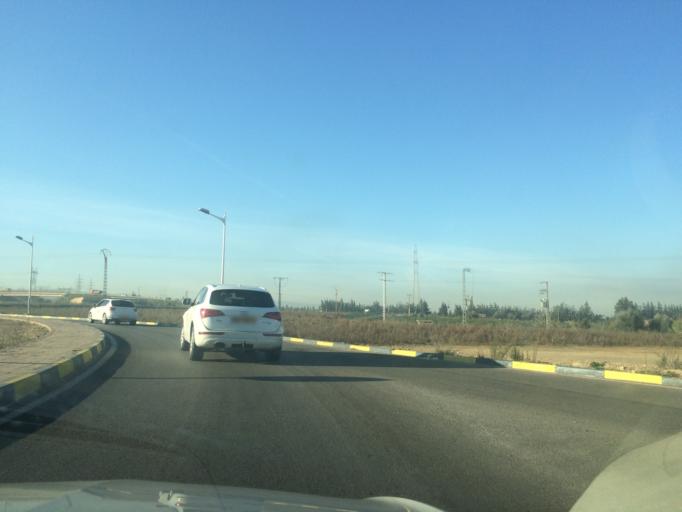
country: DZ
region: Chlef
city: Oued Sly
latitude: 36.0927
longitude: 1.1991
